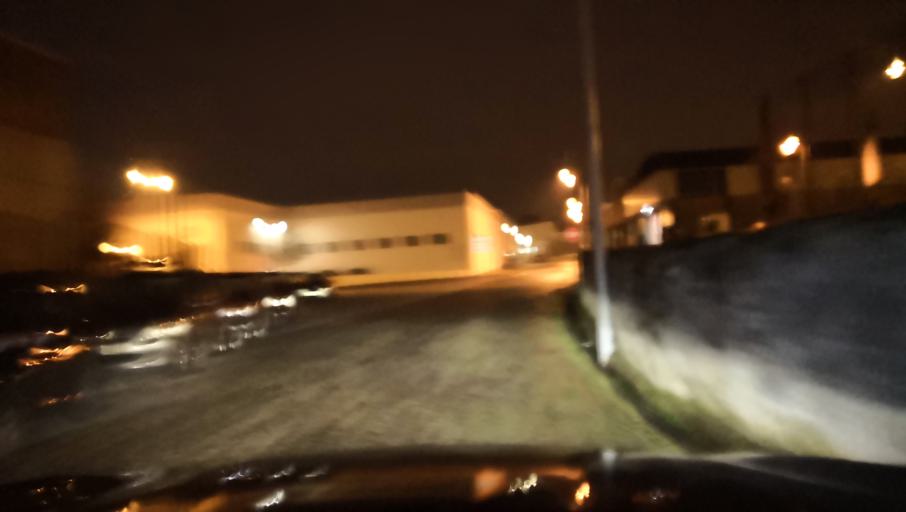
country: PT
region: Porto
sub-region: Matosinhos
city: Guifoes
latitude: 41.2029
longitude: -8.6853
